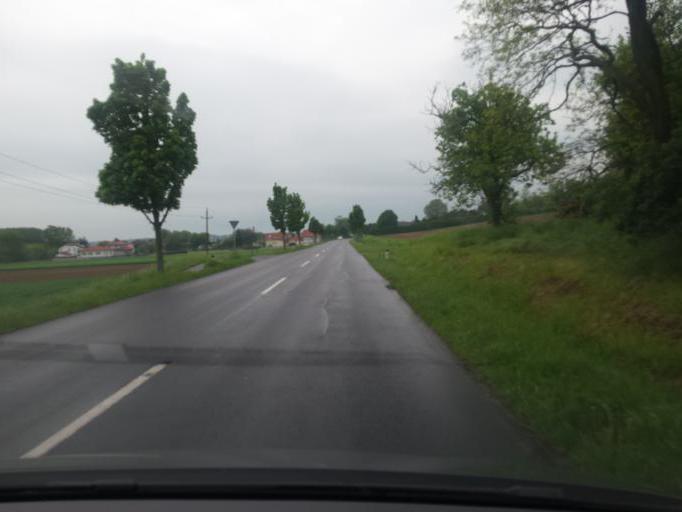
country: AT
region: Burgenland
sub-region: Politischer Bezirk Oberpullendorf
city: Mannersdorf an der Rabnitz
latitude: 47.4668
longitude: 16.5678
